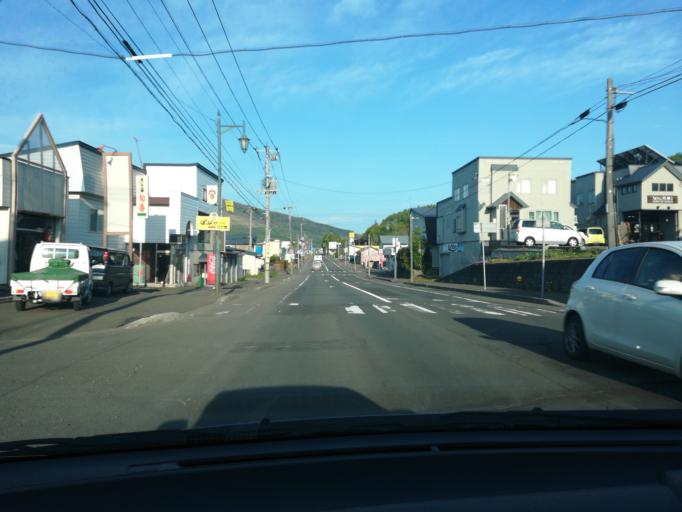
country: JP
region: Hokkaido
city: Shimo-furano
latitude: 43.1631
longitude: 142.5695
